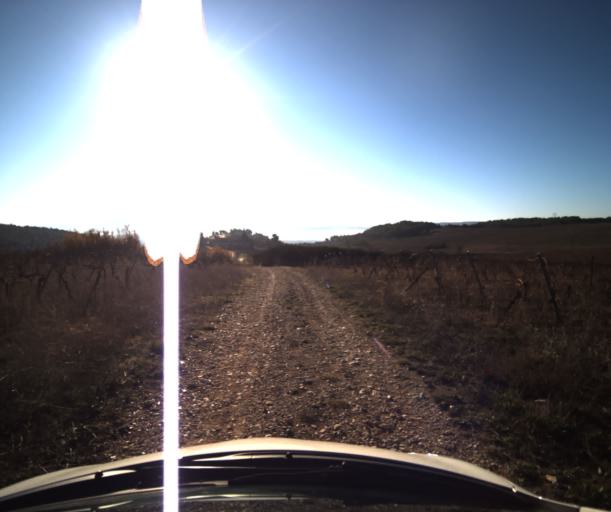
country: FR
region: Provence-Alpes-Cote d'Azur
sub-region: Departement du Vaucluse
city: Ansouis
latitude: 43.7228
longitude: 5.4896
